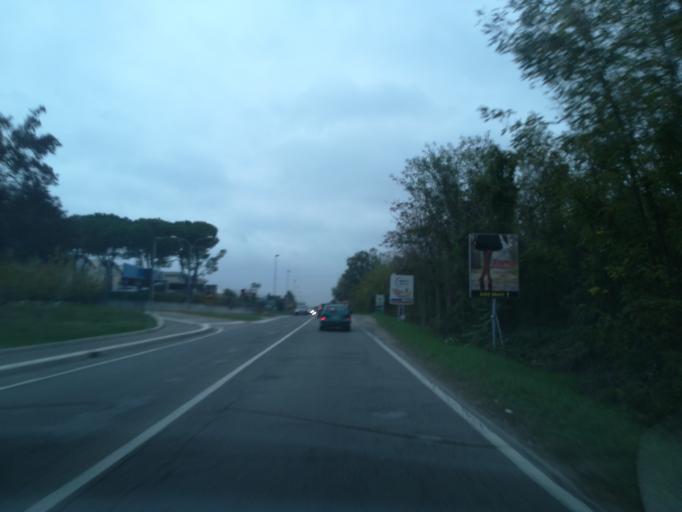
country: IT
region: Emilia-Romagna
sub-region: Provincia di Bologna
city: Toscanella
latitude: 44.3798
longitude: 11.6464
